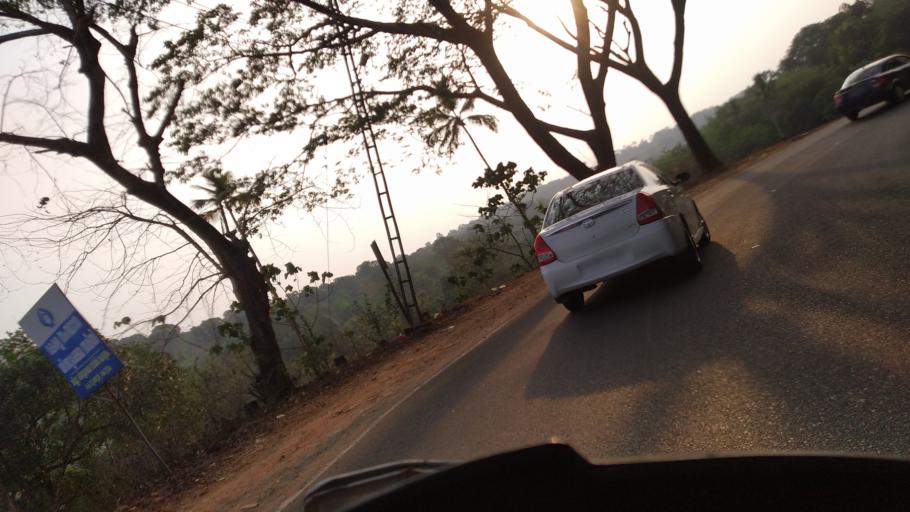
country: IN
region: Kerala
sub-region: Kottayam
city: Lalam
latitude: 9.5656
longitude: 76.7116
